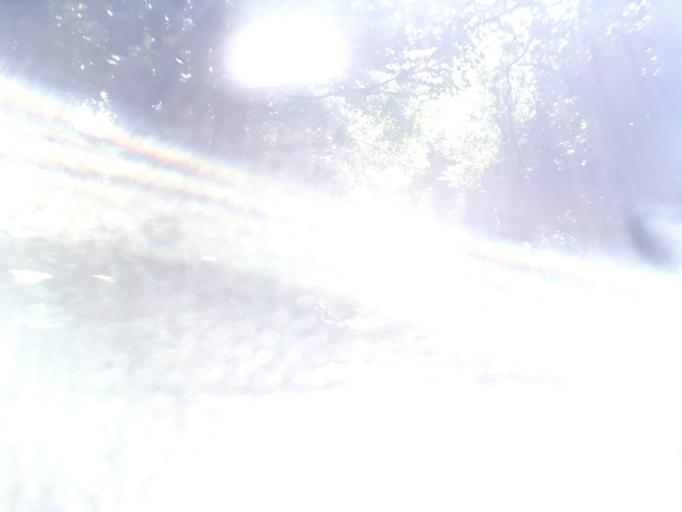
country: GB
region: England
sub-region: Gloucestershire
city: Tetbury
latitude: 51.6473
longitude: -2.1749
